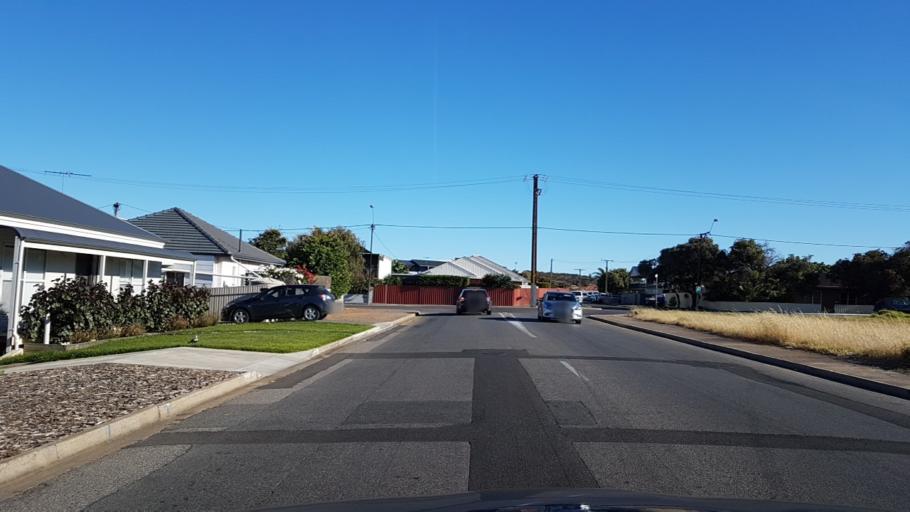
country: AU
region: South Australia
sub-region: Adelaide
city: Port Noarlunga
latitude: -35.1316
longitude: 138.4731
